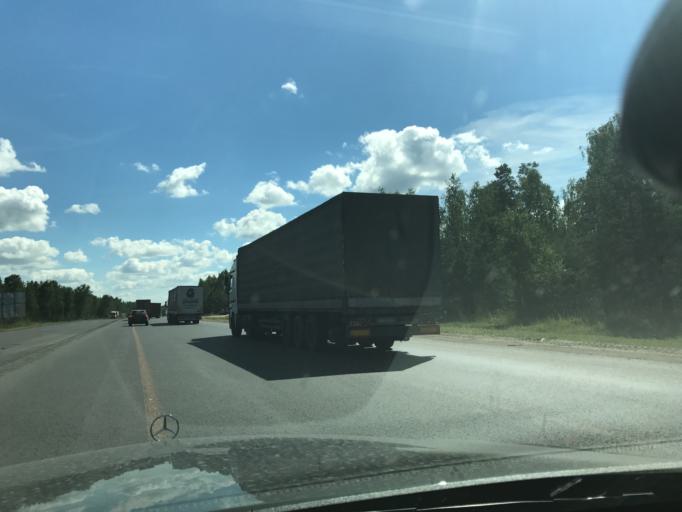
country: RU
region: Nizjnij Novgorod
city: Gorbatovka
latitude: 56.2967
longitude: 43.6926
